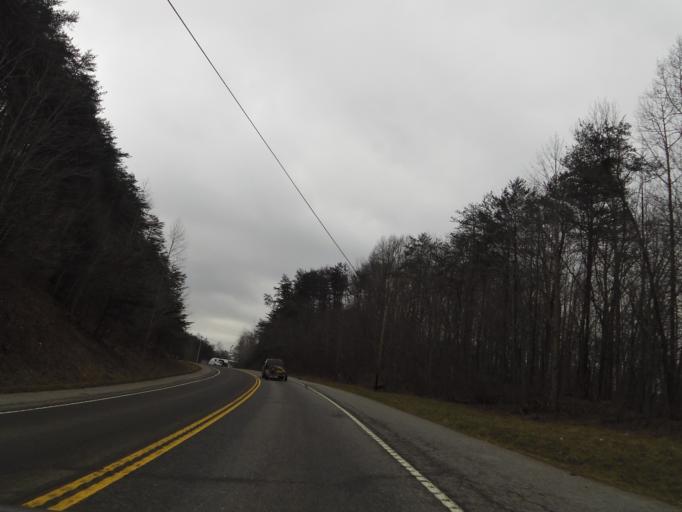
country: US
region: Tennessee
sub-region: Campbell County
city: Jacksboro
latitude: 36.3857
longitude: -84.2566
